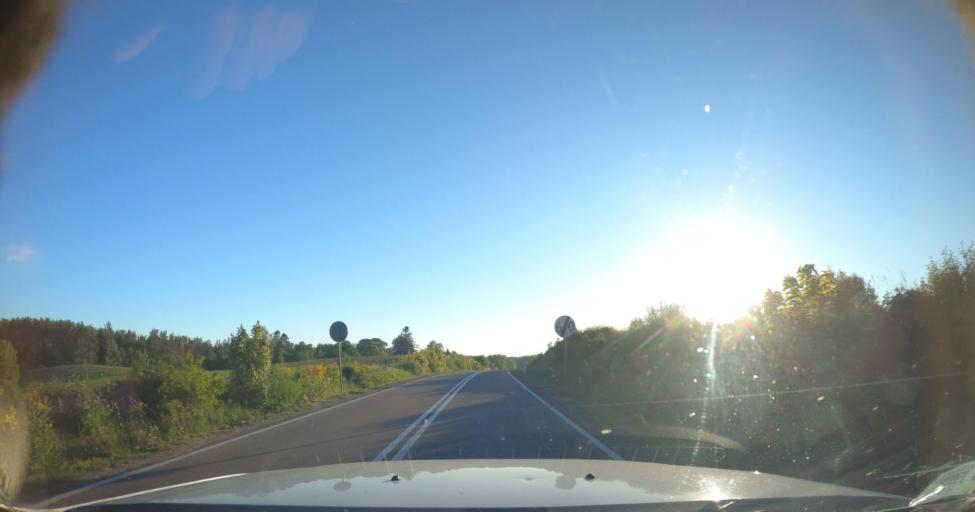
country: PL
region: Pomeranian Voivodeship
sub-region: Powiat leborski
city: Cewice
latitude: 54.3420
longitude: 17.6795
